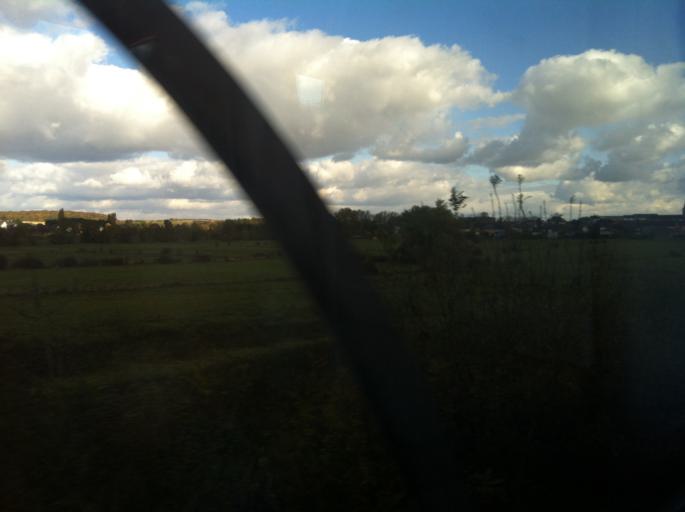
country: LU
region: Luxembourg
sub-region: Canton d'Esch-sur-Alzette
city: Bettembourg
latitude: 49.5156
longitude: 6.0872
